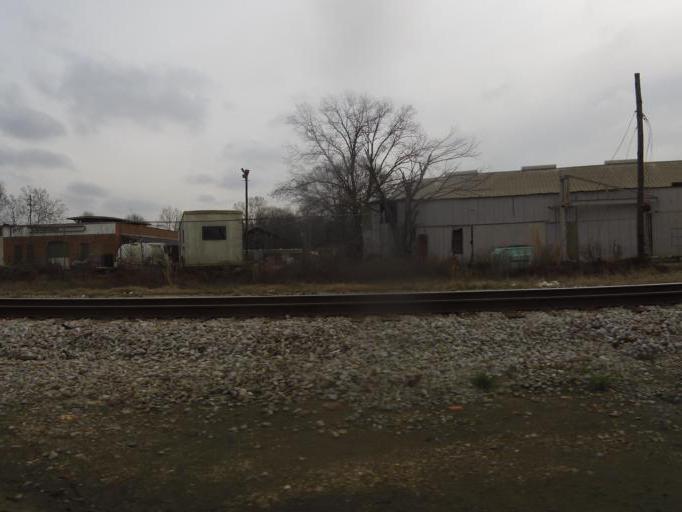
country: US
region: Alabama
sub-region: Montgomery County
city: Montgomery
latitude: 32.3862
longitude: -86.3093
